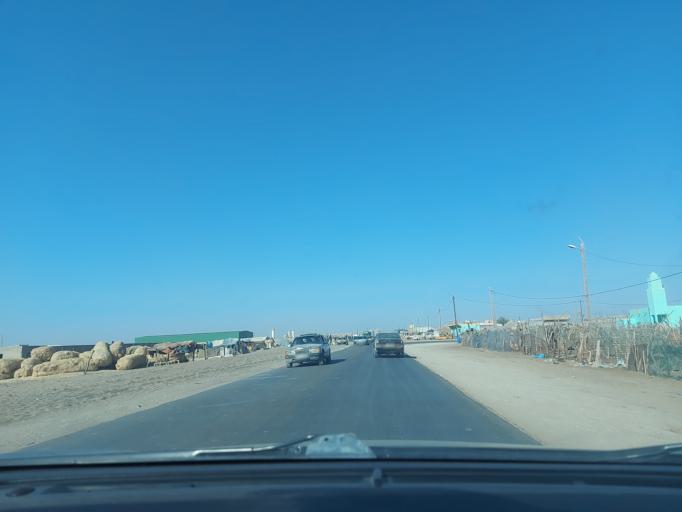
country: MR
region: Nouakchott
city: Nouakchott
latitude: 18.0540
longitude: -15.9823
